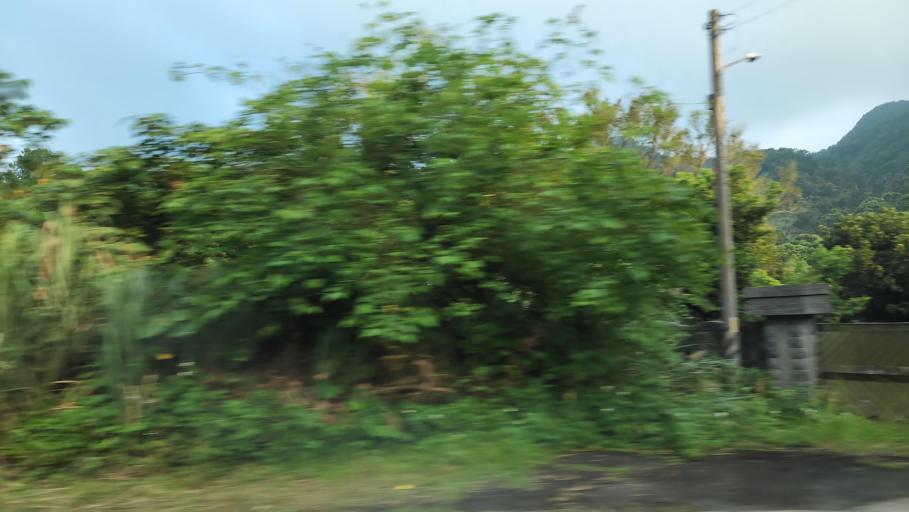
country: TW
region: Taiwan
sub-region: Keelung
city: Keelung
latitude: 25.1577
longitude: 121.6466
